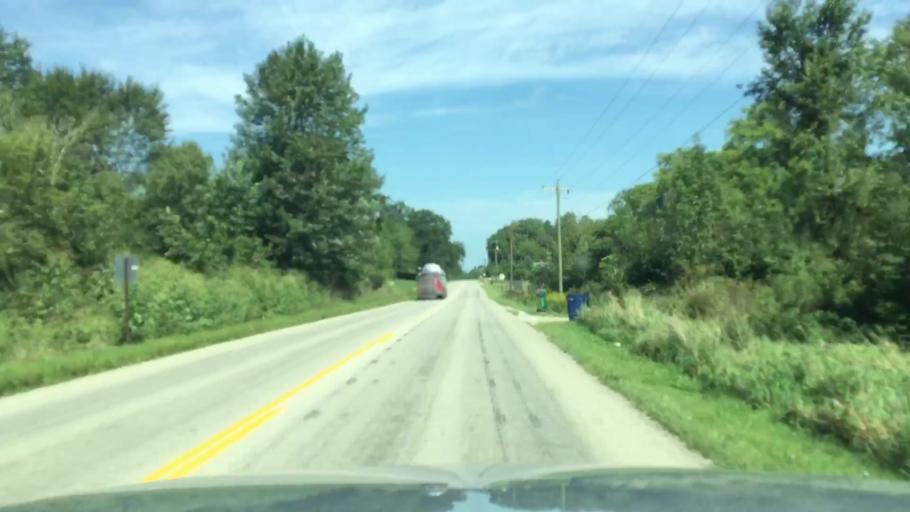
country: US
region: Michigan
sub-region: Lenawee County
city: Manitou Beach-Devils Lake
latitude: 42.0276
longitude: -84.2762
